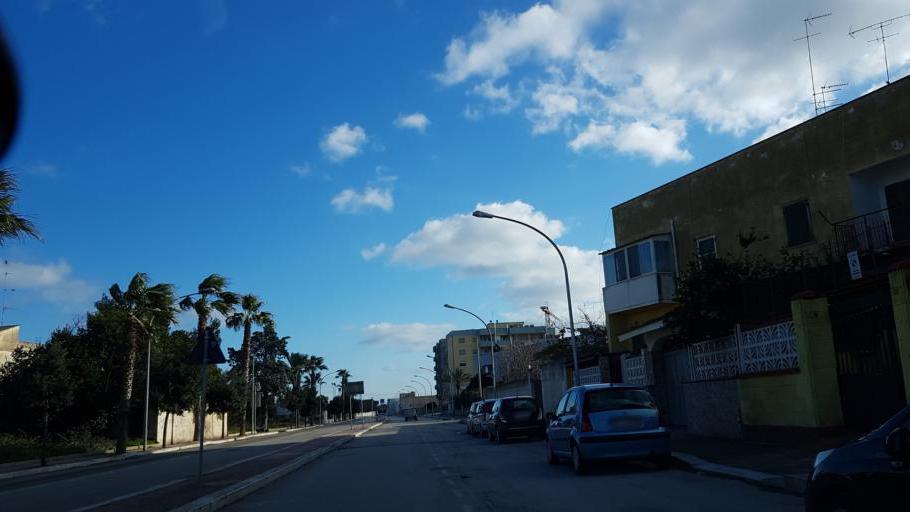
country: IT
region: Apulia
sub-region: Provincia di Brindisi
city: Brindisi
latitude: 40.6500
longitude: 17.9182
